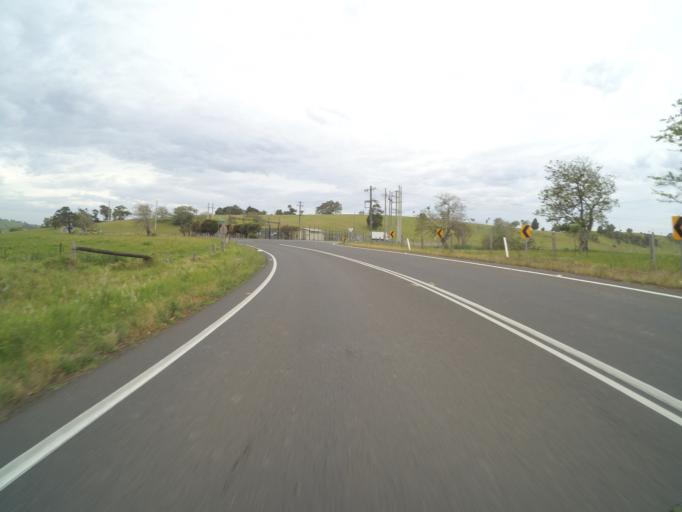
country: AU
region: New South Wales
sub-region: Kiama
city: Jamberoo
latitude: -34.6547
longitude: 150.8103
